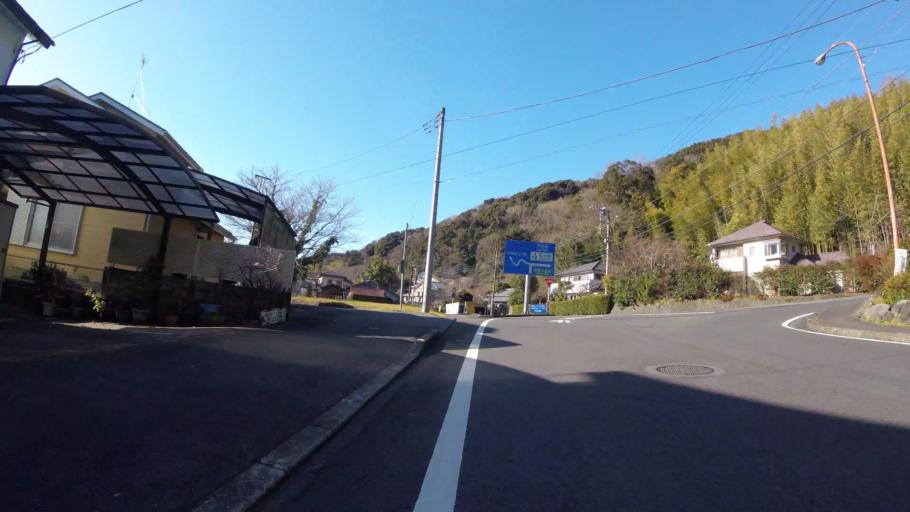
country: JP
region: Shizuoka
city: Heda
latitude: 34.9706
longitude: 138.9182
